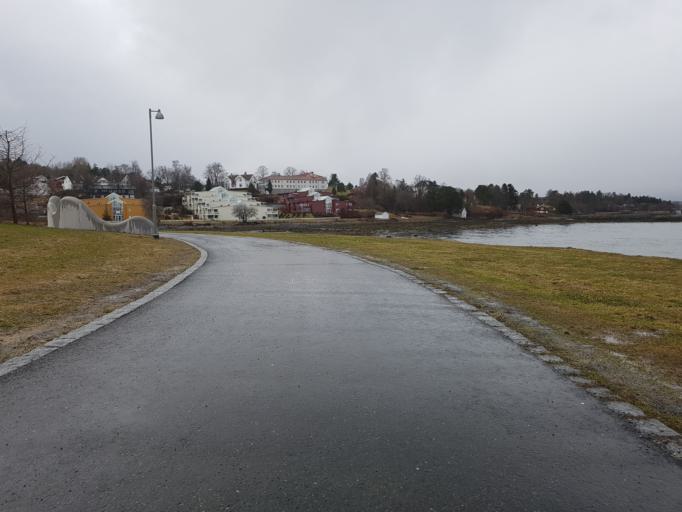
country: NO
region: Sor-Trondelag
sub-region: Trondheim
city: Trondheim
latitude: 63.4367
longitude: 10.5011
